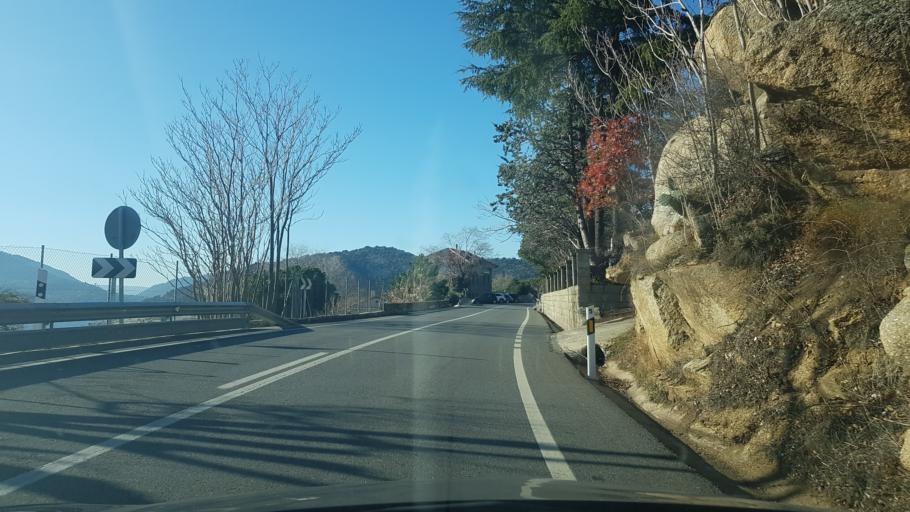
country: ES
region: Castille and Leon
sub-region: Provincia de Avila
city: El Tiemblo
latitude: 40.4287
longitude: -4.5524
